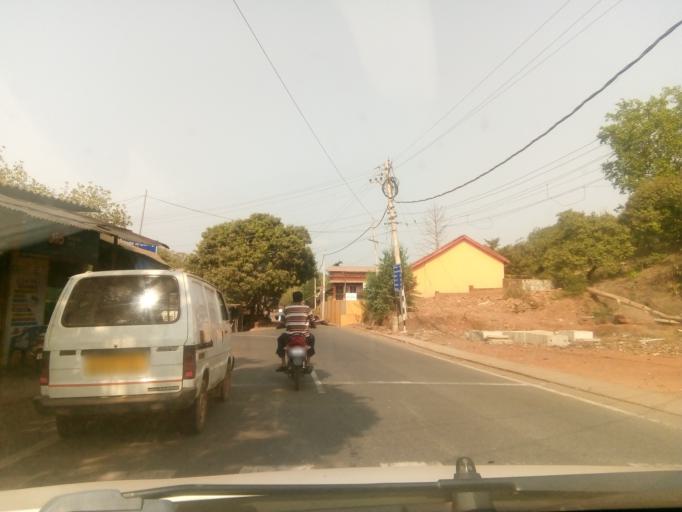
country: IN
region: Goa
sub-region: North Goa
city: Pernem
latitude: 15.7087
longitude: 73.8538
